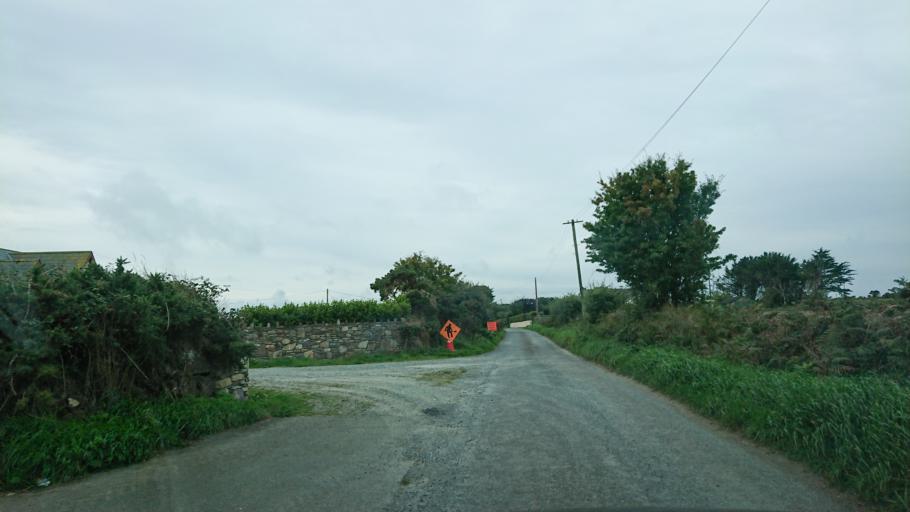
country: IE
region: Munster
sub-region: Waterford
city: Dunmore East
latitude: 52.1681
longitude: -6.9986
